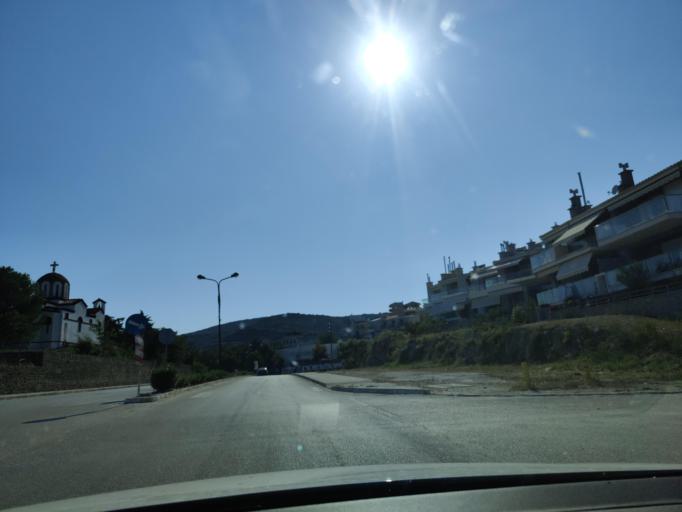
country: GR
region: East Macedonia and Thrace
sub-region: Nomos Kavalas
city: Nea Peramos
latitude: 40.8495
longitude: 24.3115
